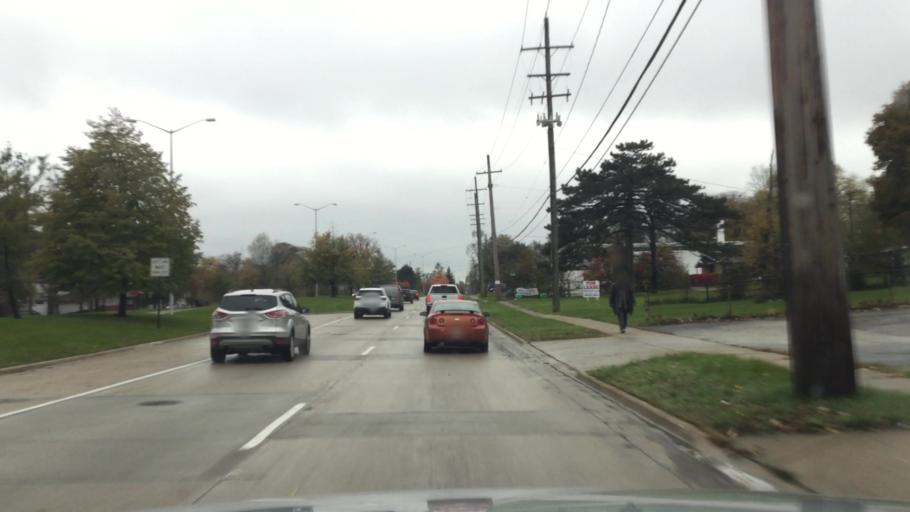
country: US
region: Michigan
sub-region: Oakland County
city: Pontiac
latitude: 42.6324
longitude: -83.3024
